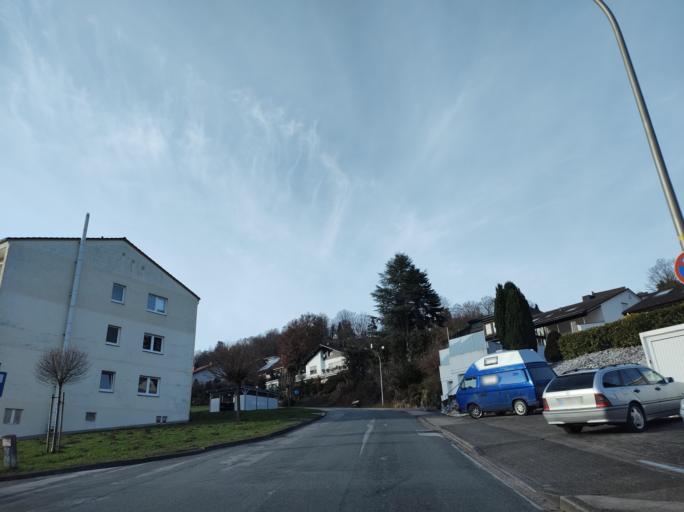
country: DE
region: North Rhine-Westphalia
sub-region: Regierungsbezirk Detmold
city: Detmold
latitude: 51.8927
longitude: 8.8705
